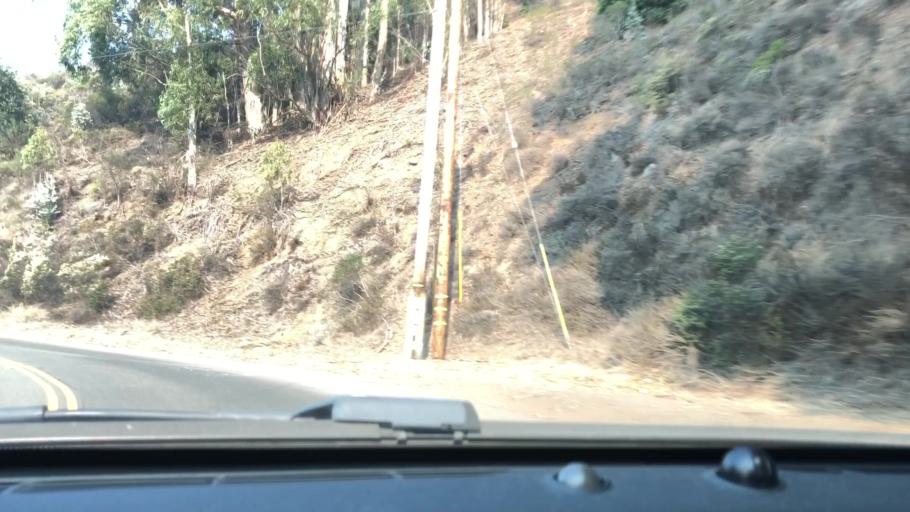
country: US
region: California
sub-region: Contra Costa County
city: Orinda
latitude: 37.8724
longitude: -122.2193
